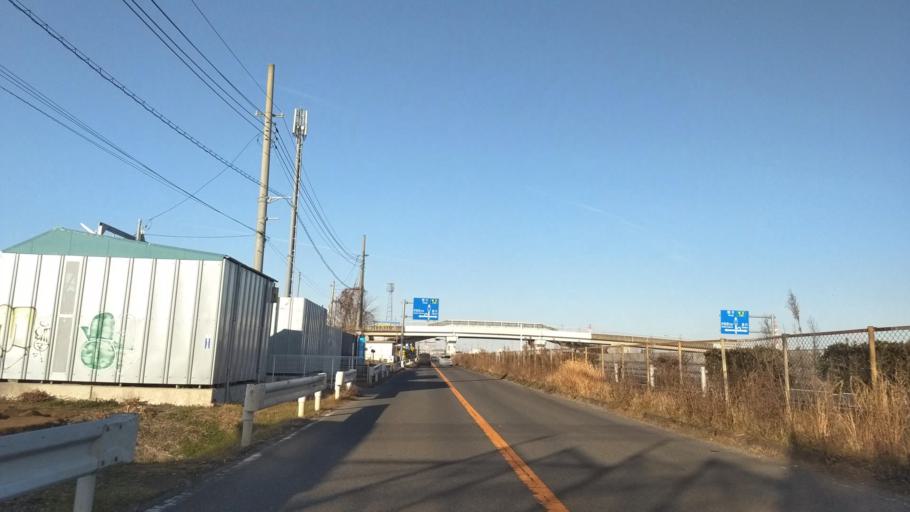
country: JP
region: Kanagawa
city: Isehara
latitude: 35.3899
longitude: 139.3326
